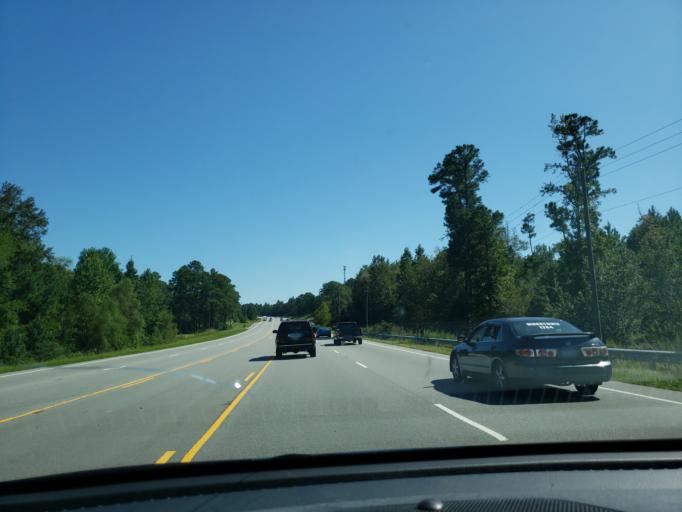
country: US
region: North Carolina
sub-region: Lee County
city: Broadway
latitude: 35.3501
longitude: -79.1083
